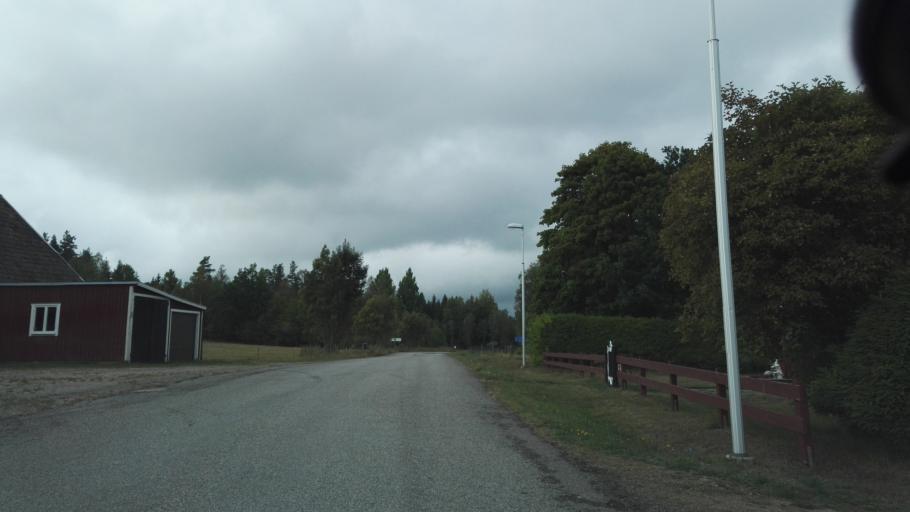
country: SE
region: Joenkoeping
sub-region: Vetlanda Kommun
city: Landsbro
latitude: 57.2622
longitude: 14.8334
